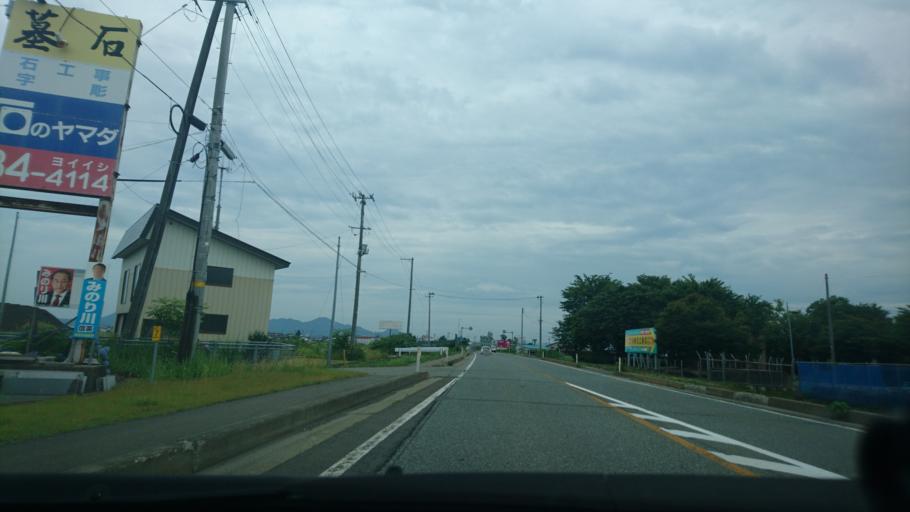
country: JP
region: Akita
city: Omagari
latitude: 39.4185
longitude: 140.5407
